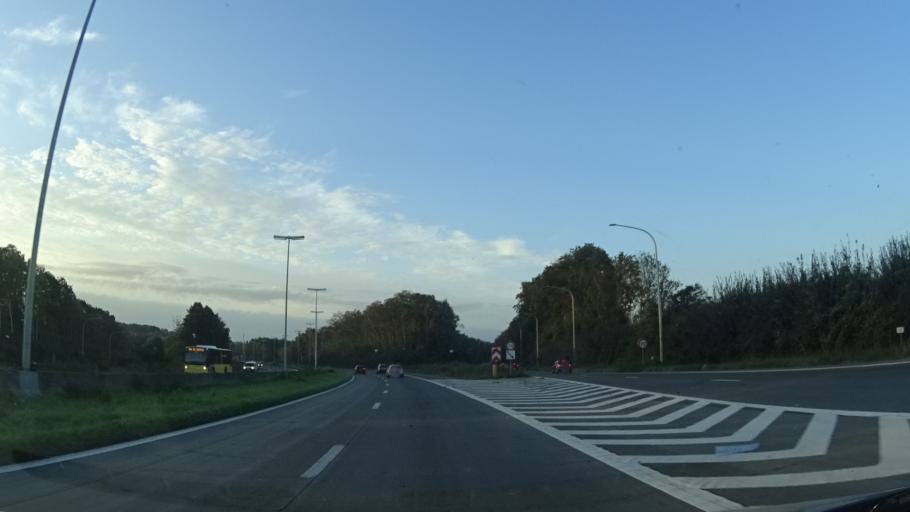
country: BE
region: Wallonia
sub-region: Province du Hainaut
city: Frameries
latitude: 50.4313
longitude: 3.9086
